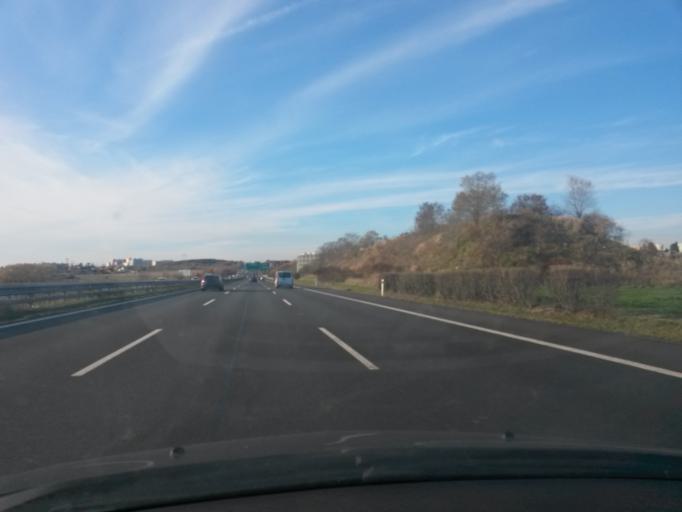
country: CZ
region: Central Bohemia
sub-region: Okres Praha-Zapad
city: Pruhonice
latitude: 50.0155
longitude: 14.5268
